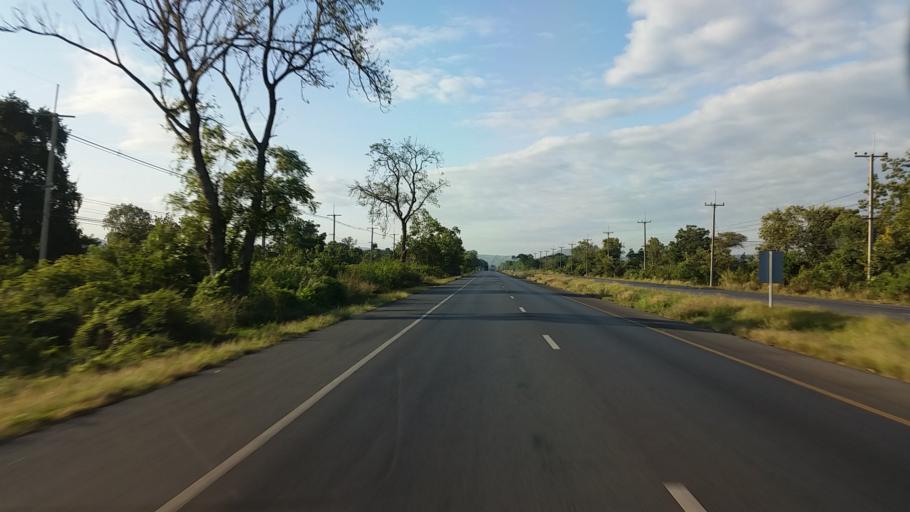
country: TH
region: Lop Buri
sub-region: Amphoe Tha Luang
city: Tha Luang
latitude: 15.0258
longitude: 100.9496
